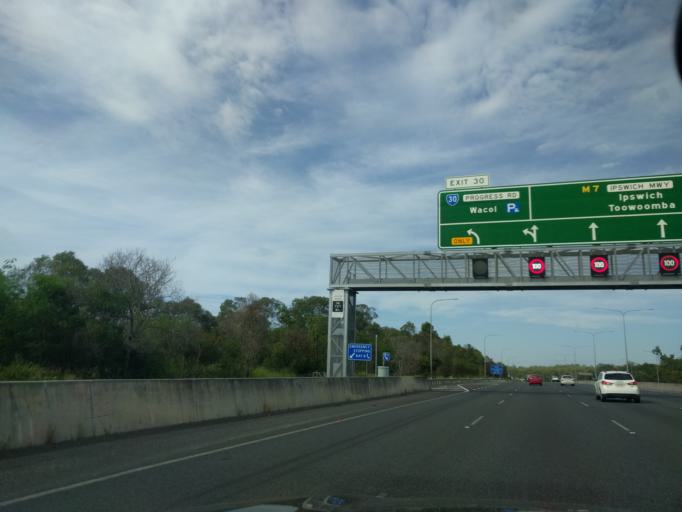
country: AU
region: Queensland
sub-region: Brisbane
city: Wacol
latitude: -27.5818
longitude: 152.9348
